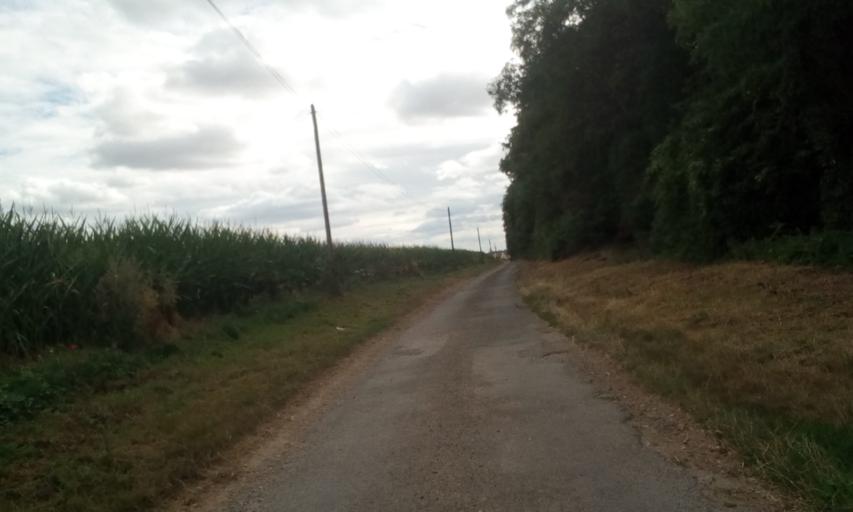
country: FR
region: Lower Normandy
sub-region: Departement du Calvados
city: Bellengreville
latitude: 49.1285
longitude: -0.1939
